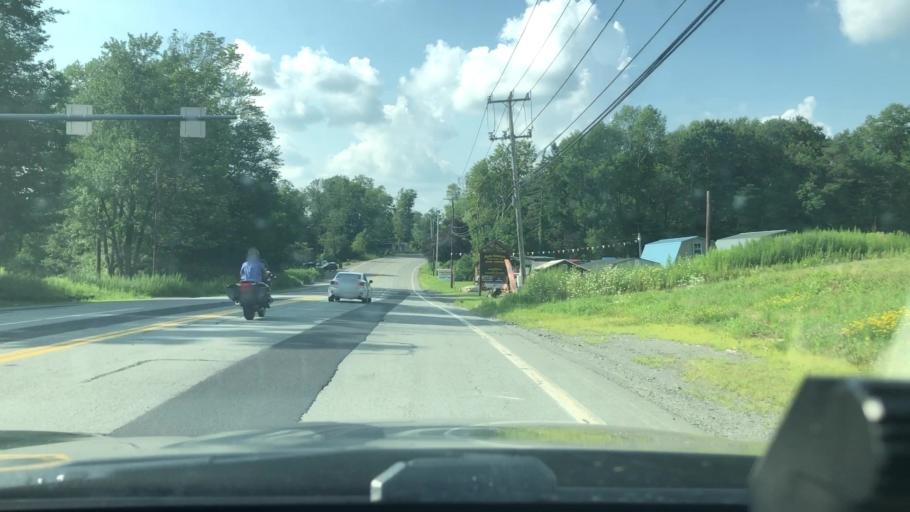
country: US
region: Pennsylvania
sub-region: Lackawanna County
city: Moscow
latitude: 41.2600
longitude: -75.5057
